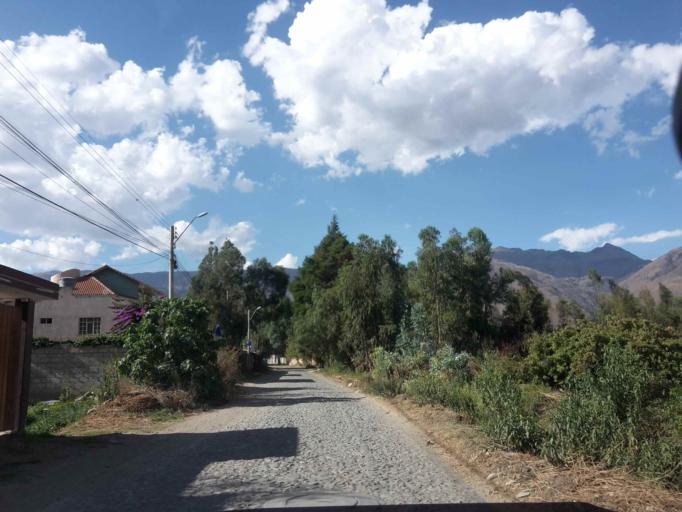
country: BO
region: Cochabamba
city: Cochabamba
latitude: -17.3663
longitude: -66.2074
